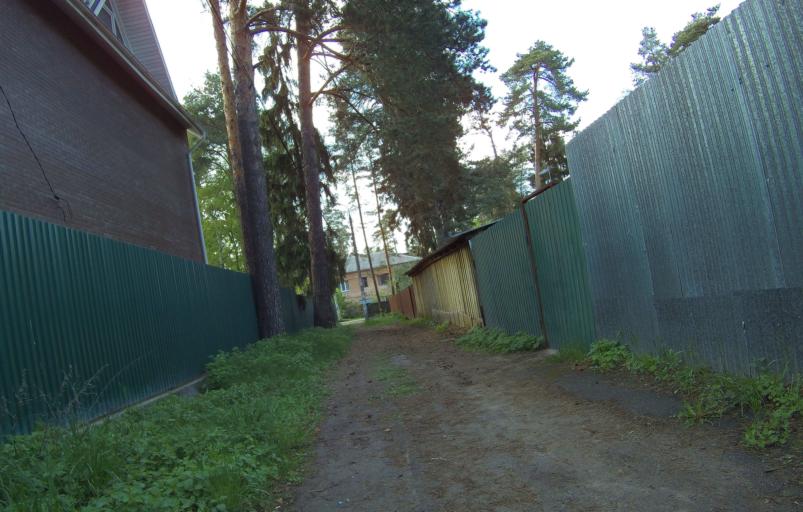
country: RU
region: Moskovskaya
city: Kratovo
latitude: 55.5944
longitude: 38.1652
